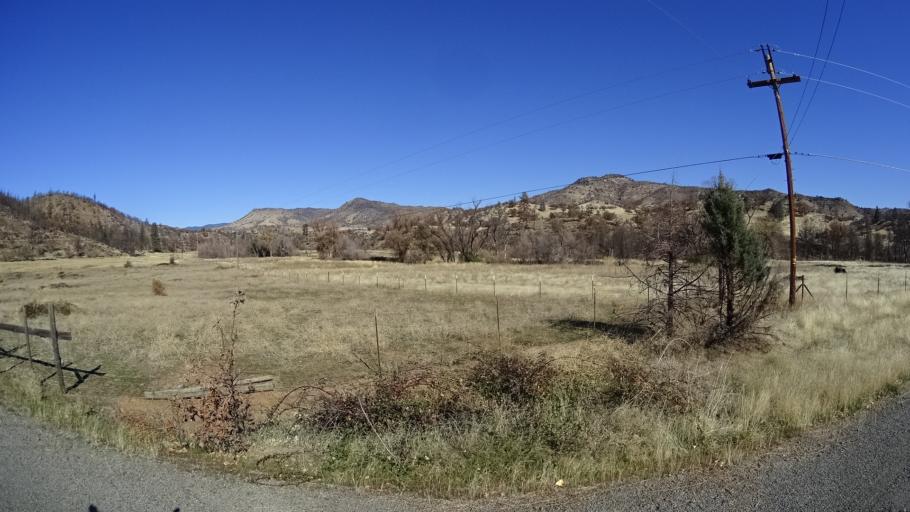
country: US
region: California
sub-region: Siskiyou County
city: Yreka
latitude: 41.9324
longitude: -122.5900
